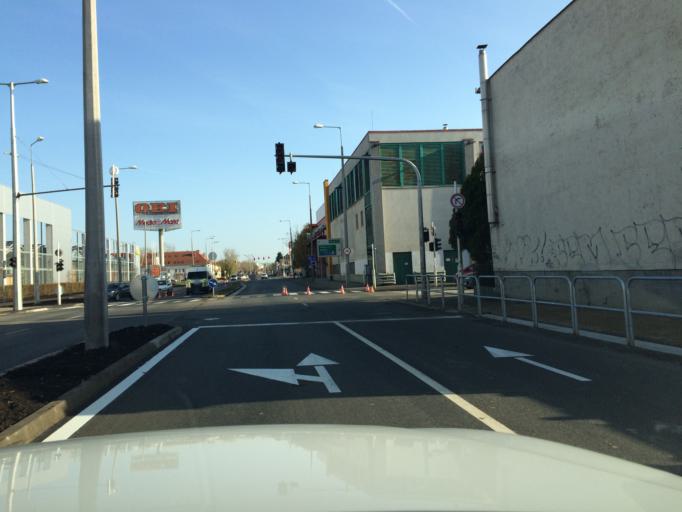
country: HU
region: Szabolcs-Szatmar-Bereg
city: Nyiregyhaza
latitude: 47.9569
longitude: 21.7255
